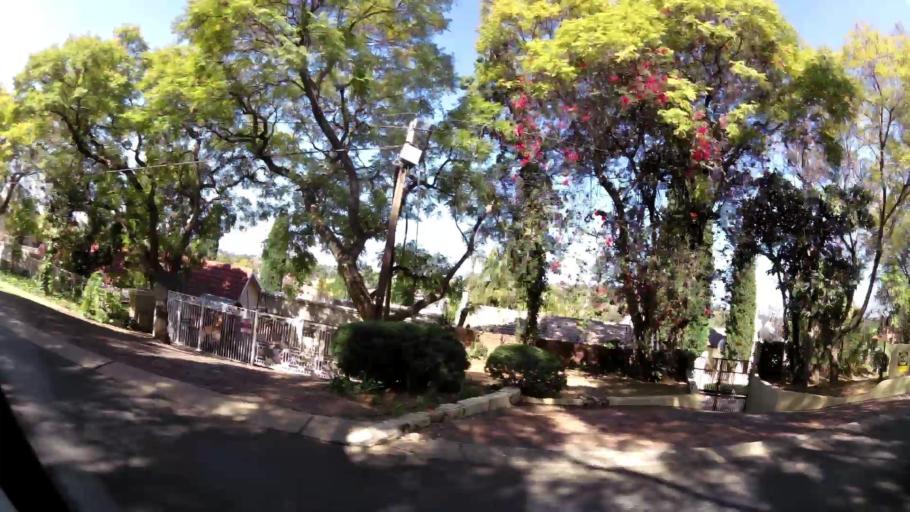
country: ZA
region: Gauteng
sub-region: City of Tshwane Metropolitan Municipality
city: Pretoria
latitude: -25.7859
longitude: 28.2477
